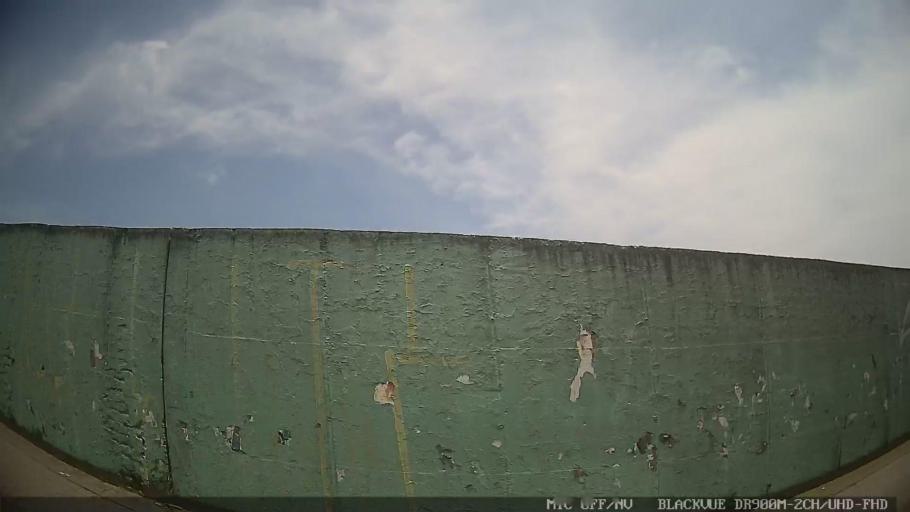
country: BR
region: Sao Paulo
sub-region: Ferraz De Vasconcelos
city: Ferraz de Vasconcelos
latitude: -23.5450
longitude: -46.3754
